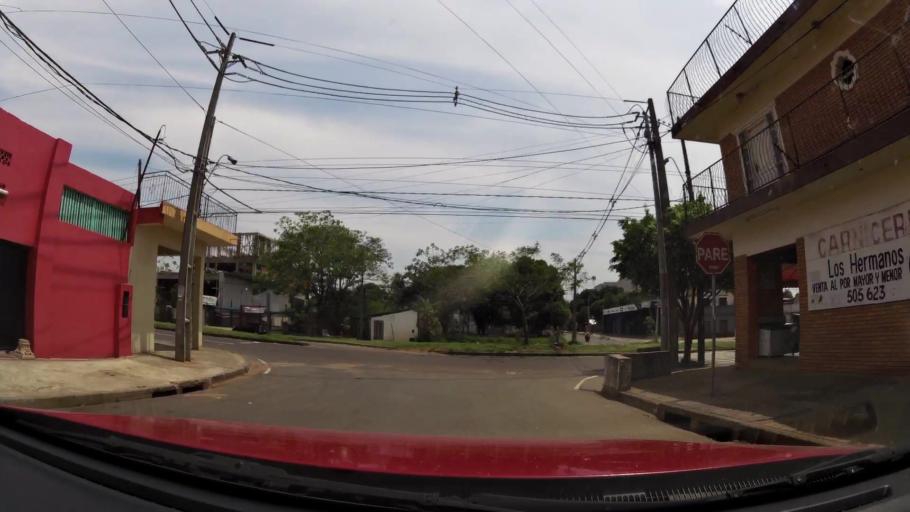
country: PY
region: Central
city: Fernando de la Mora
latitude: -25.3168
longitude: -57.5574
